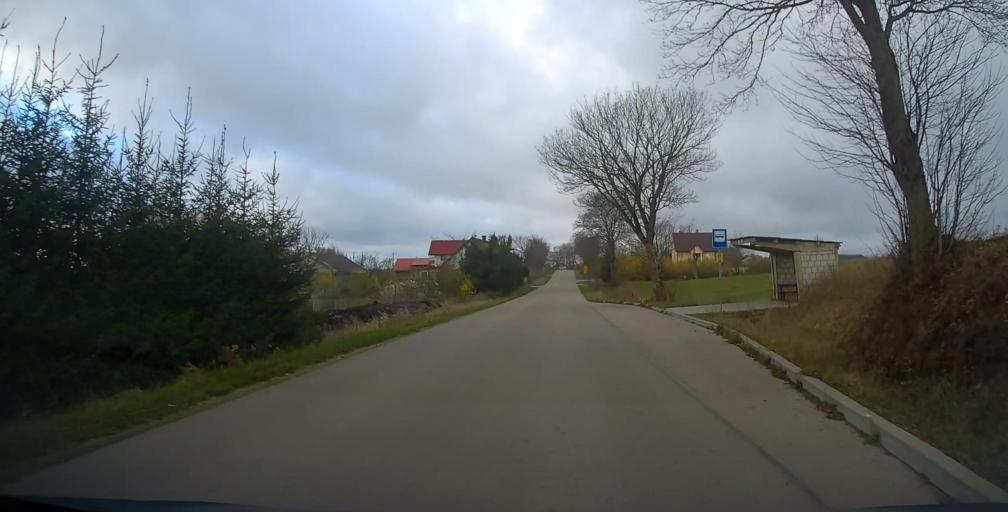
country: PL
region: Podlasie
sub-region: Suwalki
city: Suwalki
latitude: 54.3167
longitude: 22.8696
